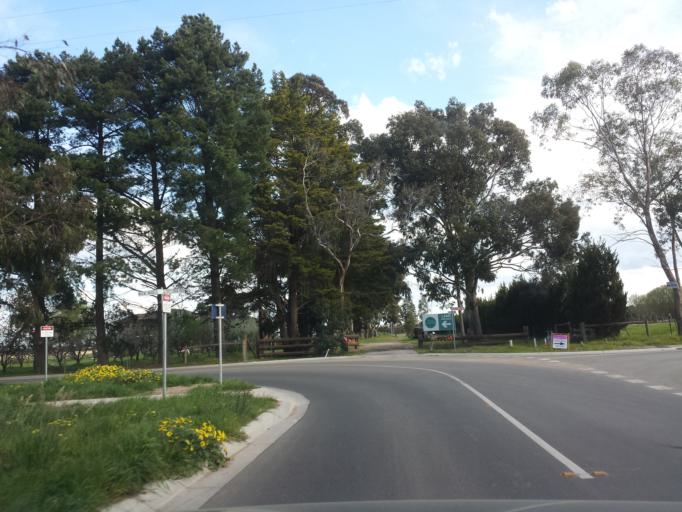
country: AU
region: Victoria
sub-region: Cardinia
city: Officer
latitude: -38.0656
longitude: 145.3874
